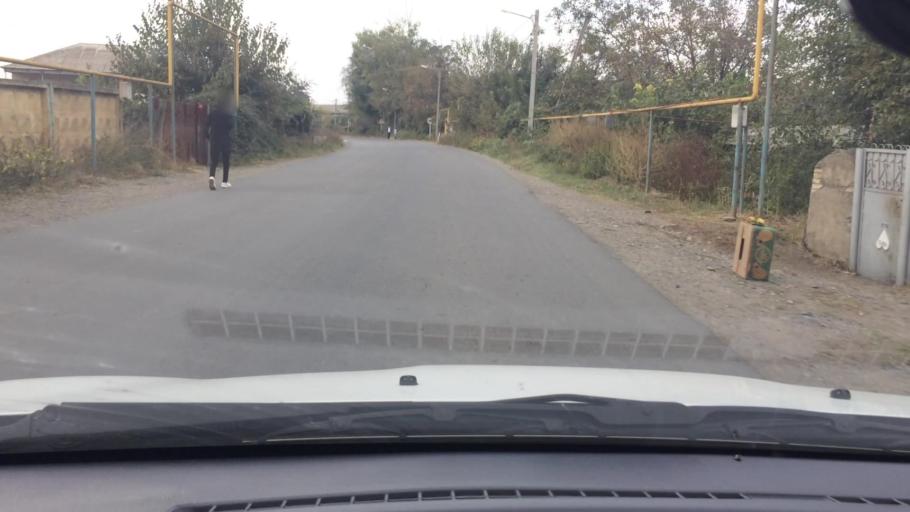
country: GE
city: Naghvarevi
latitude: 41.3526
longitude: 44.8628
